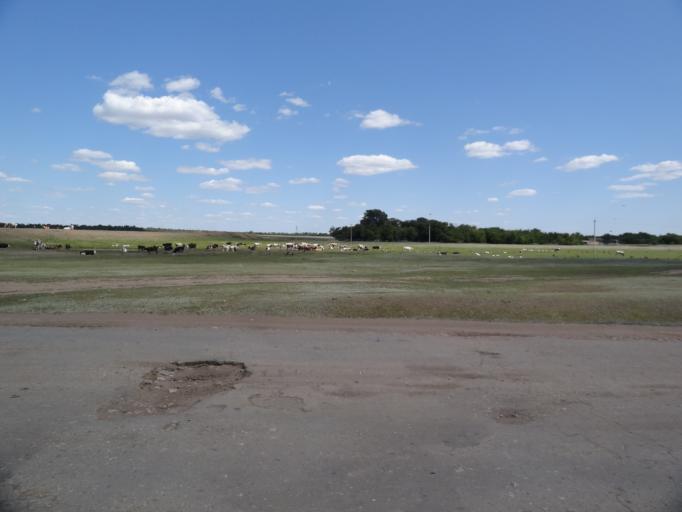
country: RU
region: Saratov
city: Sovetskoye
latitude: 51.2879
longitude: 46.6512
